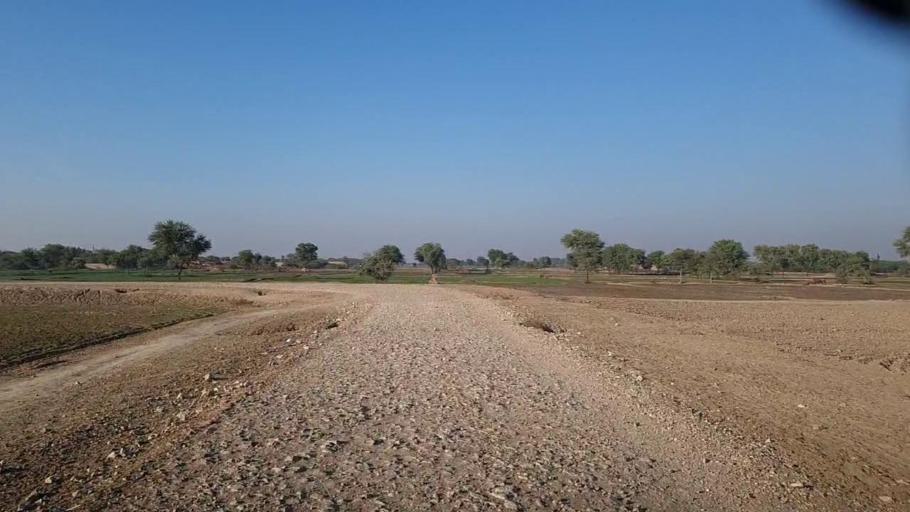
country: PK
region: Sindh
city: Pad Idan
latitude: 26.7337
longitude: 68.3492
